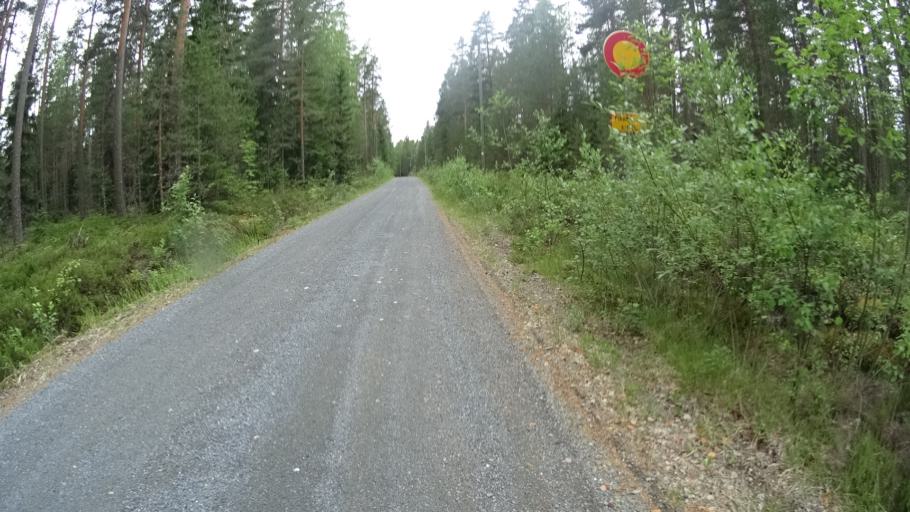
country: FI
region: Uusimaa
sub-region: Helsinki
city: Karkkila
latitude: 60.6031
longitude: 24.1581
